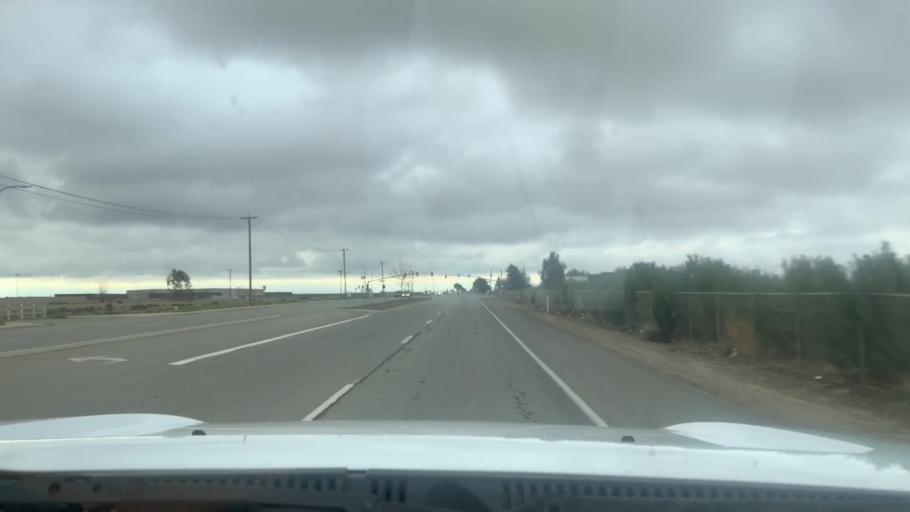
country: US
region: California
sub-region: Kern County
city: Shafter
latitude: 35.4998
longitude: -119.1763
